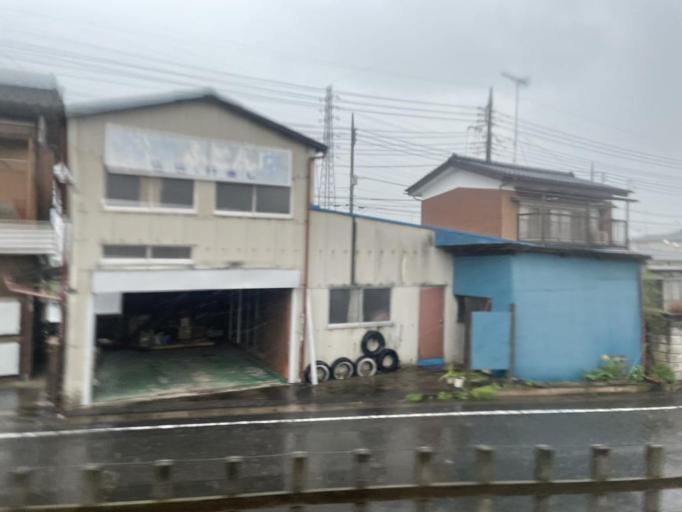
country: JP
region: Gunma
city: Tatebayashi
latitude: 36.2563
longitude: 139.5202
